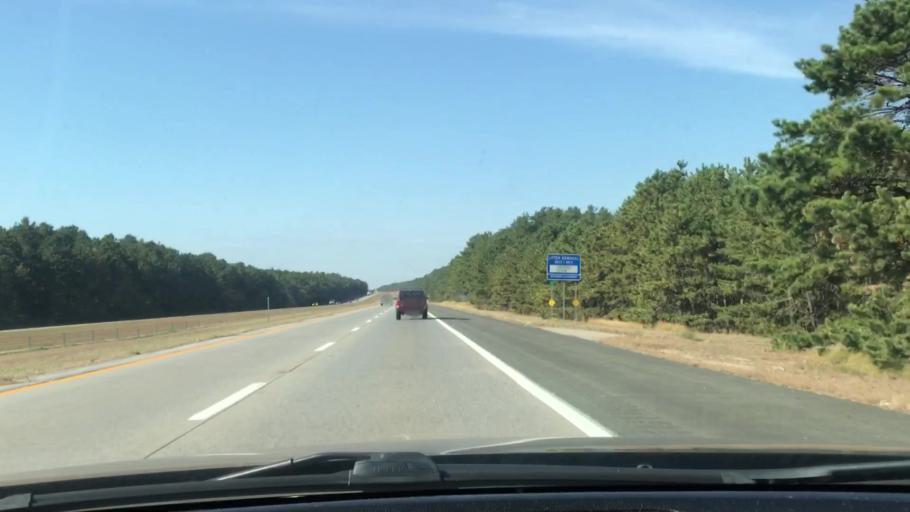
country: US
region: New York
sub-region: Suffolk County
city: East Quogue
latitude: 40.8754
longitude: -72.5827
